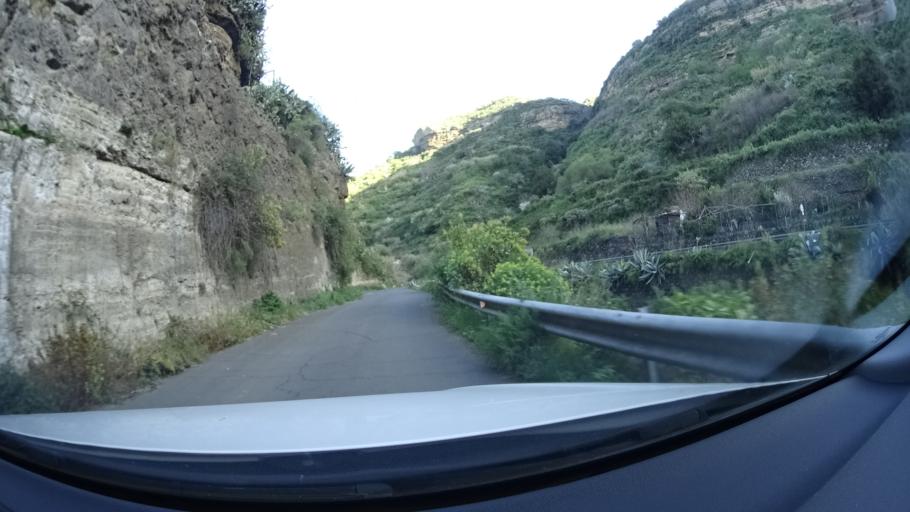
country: ES
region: Canary Islands
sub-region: Provincia de Las Palmas
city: Artenara
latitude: 28.0455
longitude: -15.6642
